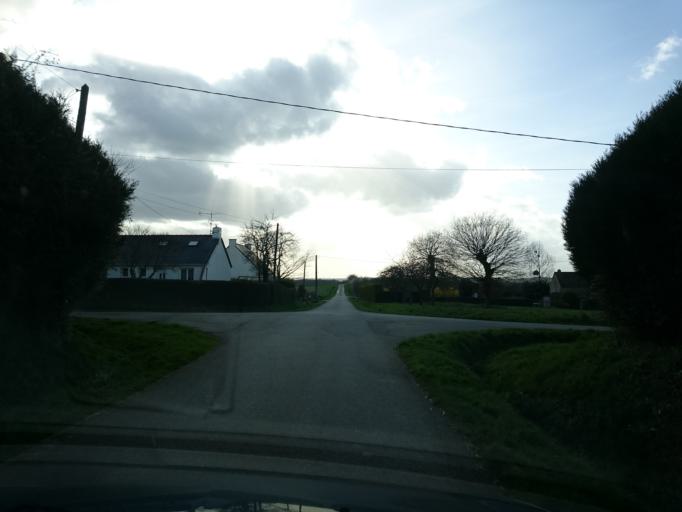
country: FR
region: Brittany
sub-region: Departement d'Ille-et-Vilaine
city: Crevin
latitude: 47.9203
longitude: -1.6496
